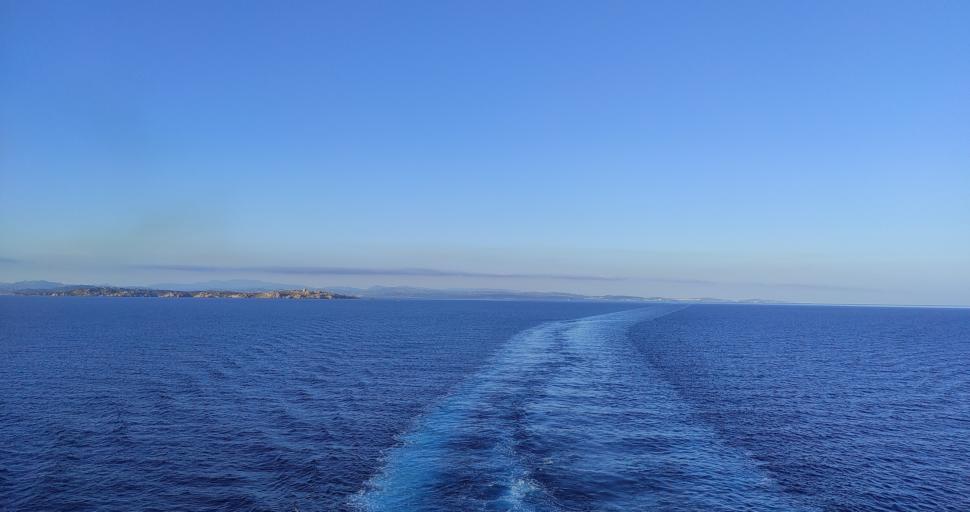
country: IT
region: Sardinia
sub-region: Provincia di Olbia-Tempio
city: La Maddalena
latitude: 41.3499
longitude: 9.3608
